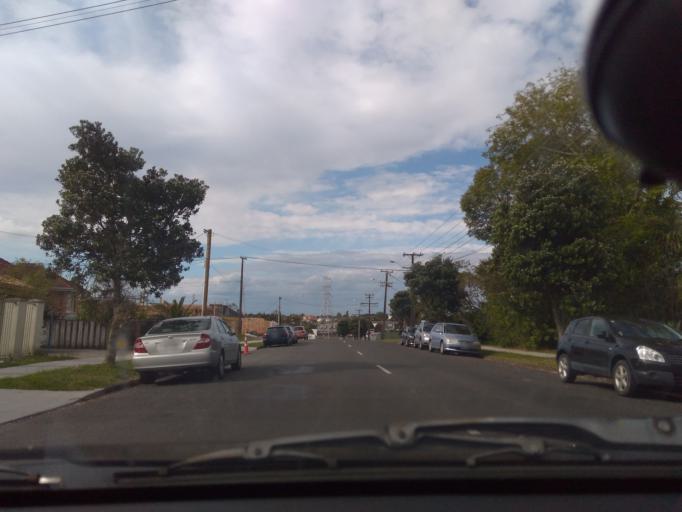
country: NZ
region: Auckland
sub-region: Auckland
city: Waitakere
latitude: -36.9048
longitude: 174.6839
